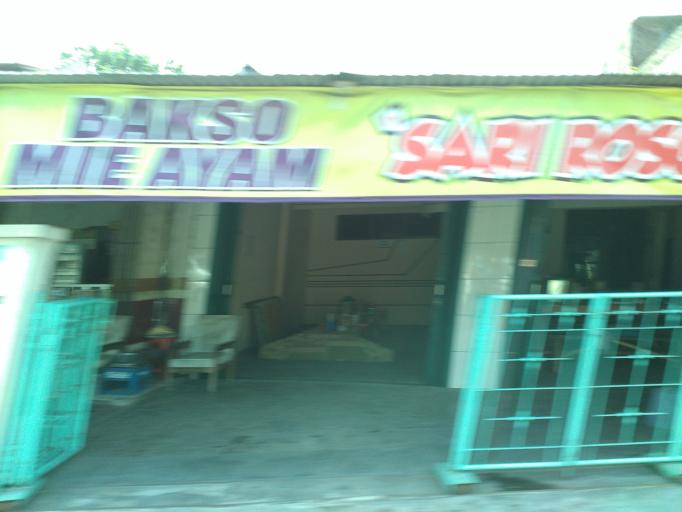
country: ID
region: Central Java
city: Candi Prambanan
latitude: -7.7463
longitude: 110.5257
